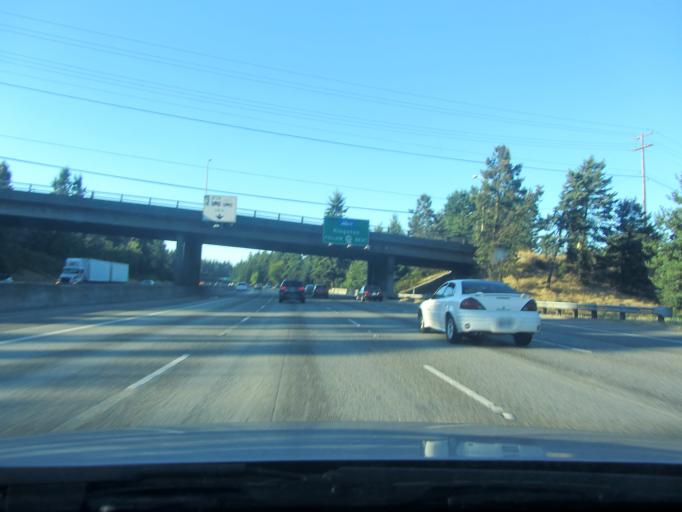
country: US
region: Washington
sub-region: King County
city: Shoreline
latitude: 47.7628
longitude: -122.3238
